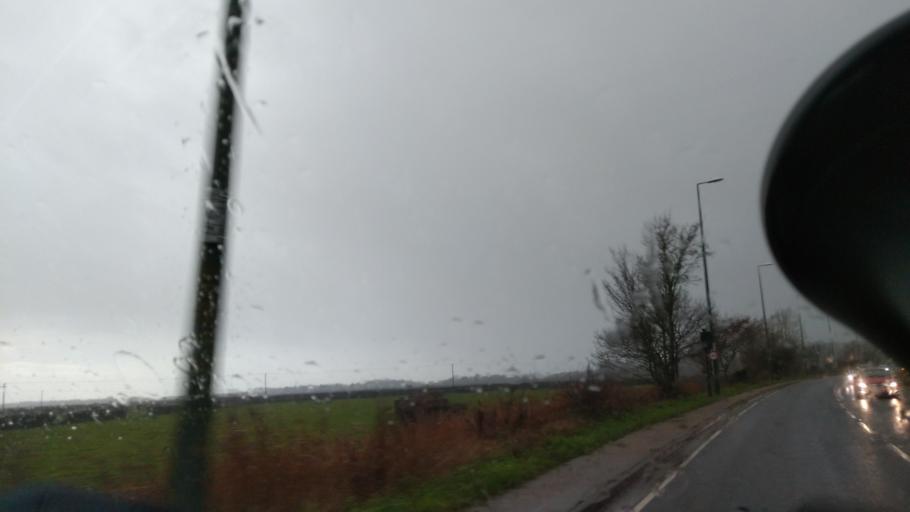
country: GB
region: England
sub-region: West Sussex
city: Arundel
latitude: 50.8497
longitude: -0.5516
